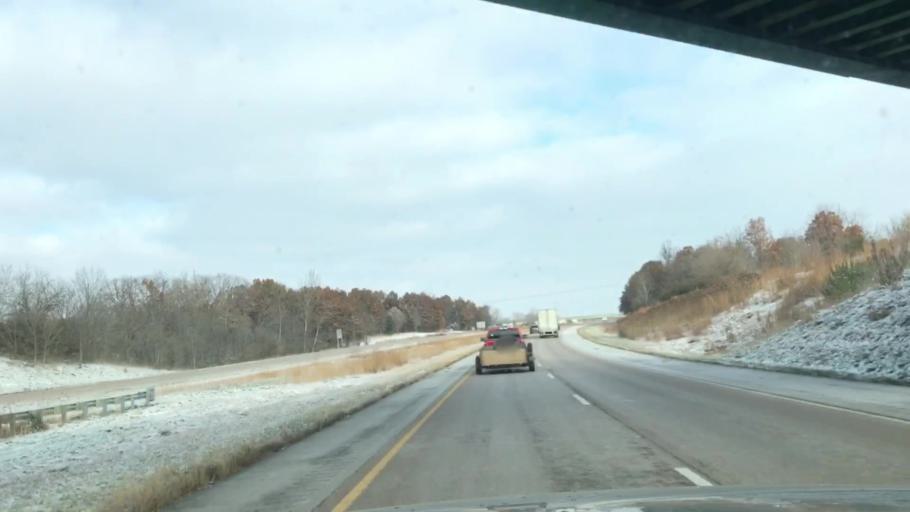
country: US
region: Illinois
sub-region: Macoupin County
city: Staunton
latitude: 39.0363
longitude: -89.7551
